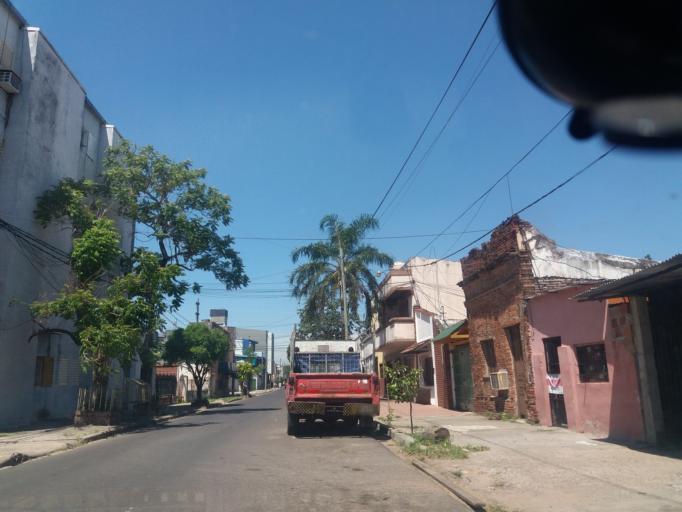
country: AR
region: Corrientes
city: Corrientes
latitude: -27.4766
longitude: -58.8446
